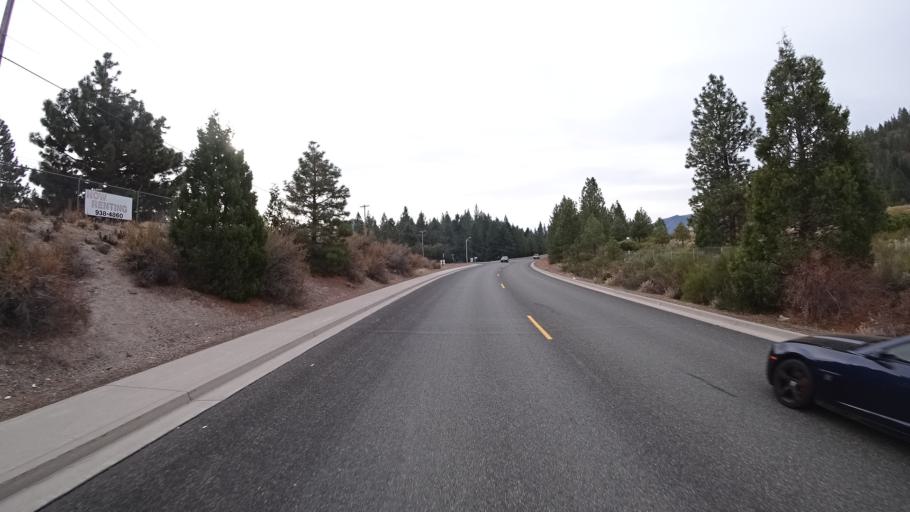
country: US
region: California
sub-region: Siskiyou County
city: Weed
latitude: 41.4103
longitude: -122.3789
